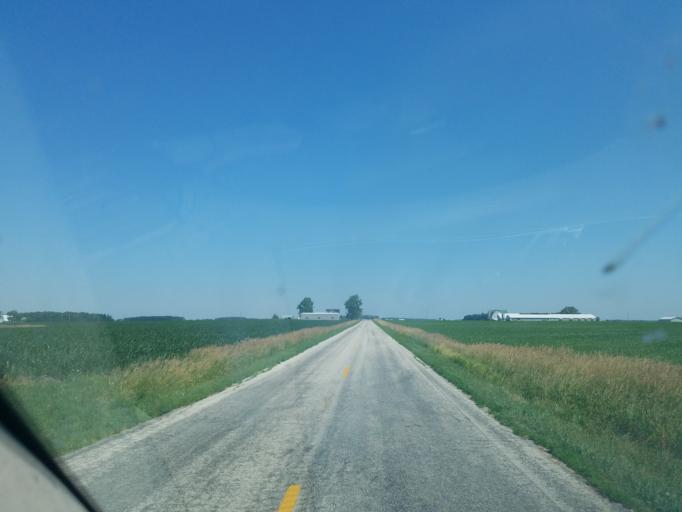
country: US
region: Ohio
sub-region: Mercer County
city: Rockford
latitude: 40.6285
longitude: -84.7086
